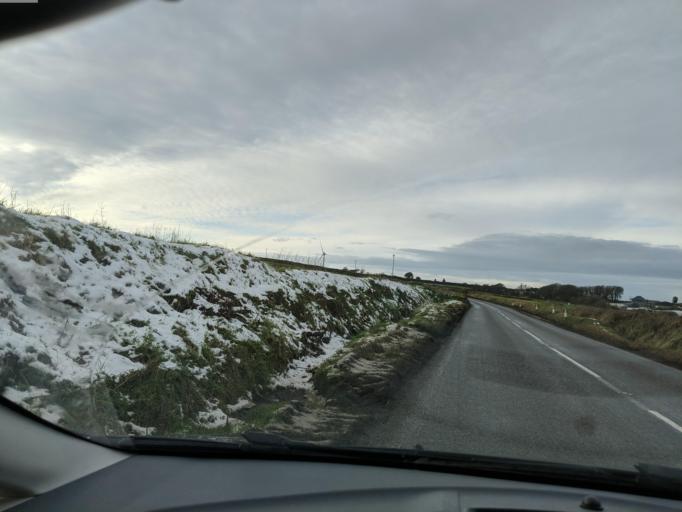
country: GB
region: England
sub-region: Cornwall
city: Jacobstow
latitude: 50.6638
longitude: -4.5846
